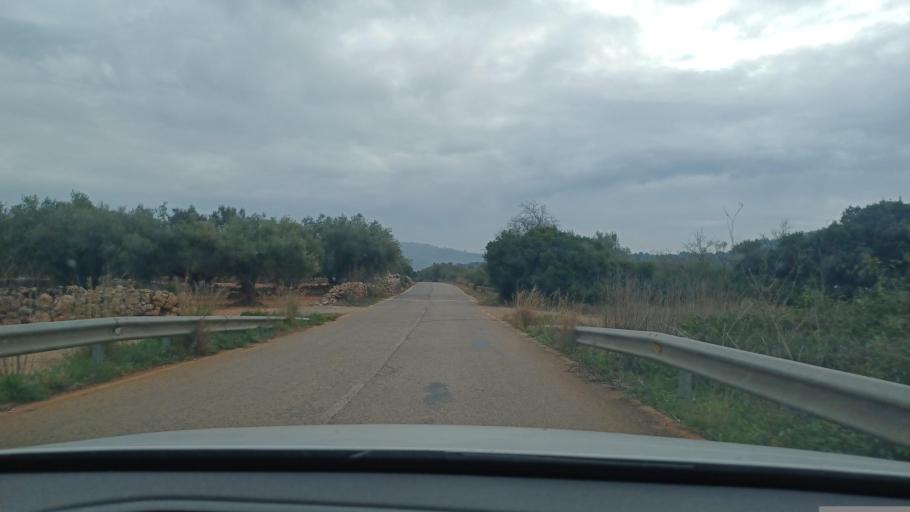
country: ES
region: Catalonia
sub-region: Provincia de Tarragona
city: Santa Barbara
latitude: 40.6649
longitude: 0.4535
